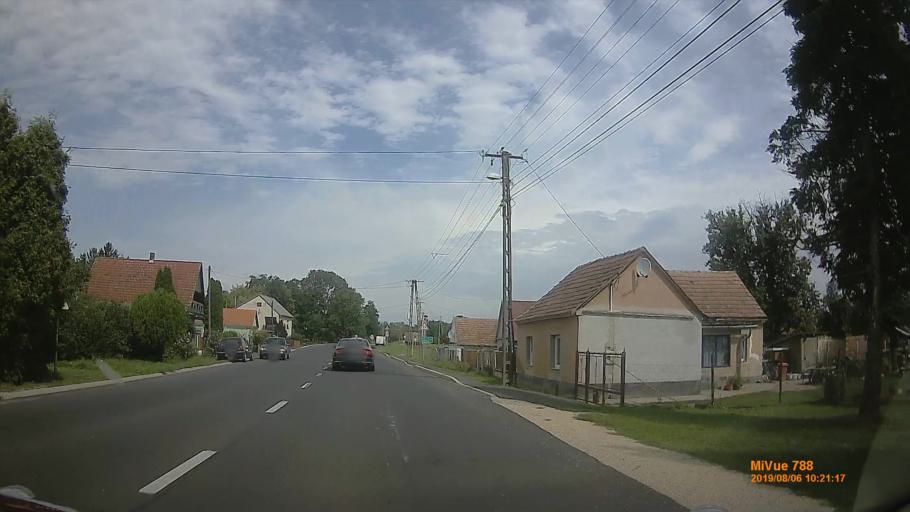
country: HU
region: Vas
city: Vasvar
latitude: 47.0651
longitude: 16.7447
